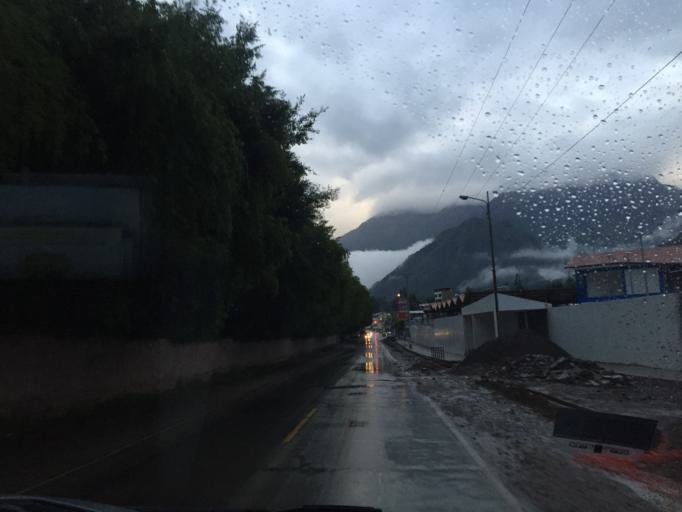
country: PE
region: Cusco
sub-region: Provincia de Urubamba
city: Urubamba
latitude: -13.3065
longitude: -72.1199
